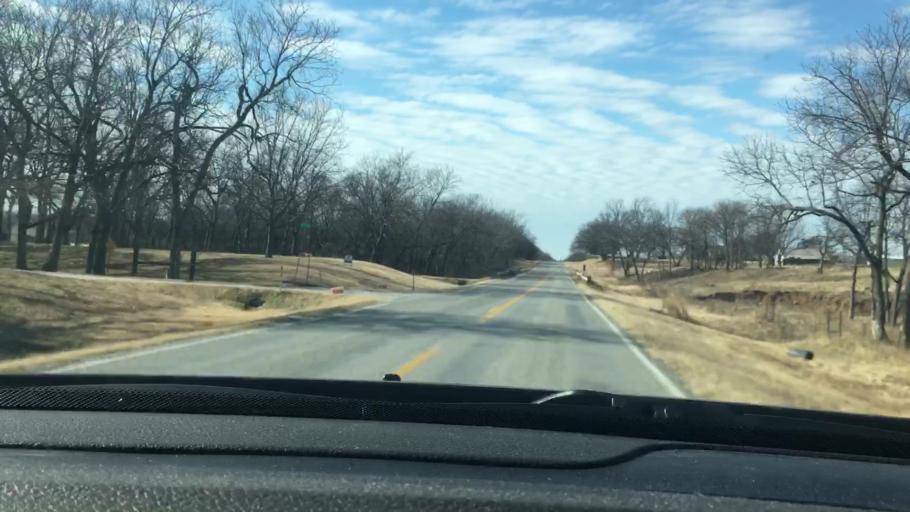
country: US
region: Oklahoma
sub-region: Garvin County
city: Wynnewood
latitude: 34.6516
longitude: -97.1172
